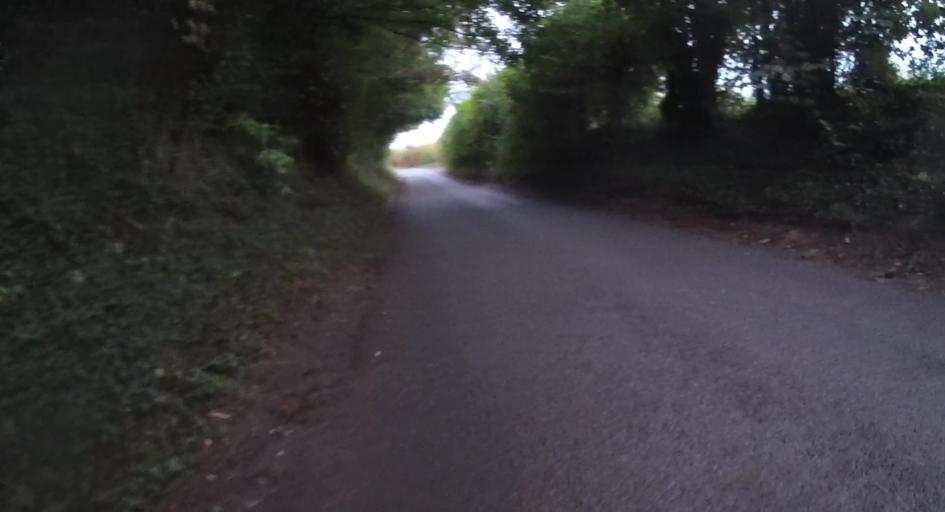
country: GB
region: England
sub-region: Hampshire
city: Tadley
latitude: 51.2992
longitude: -1.1285
